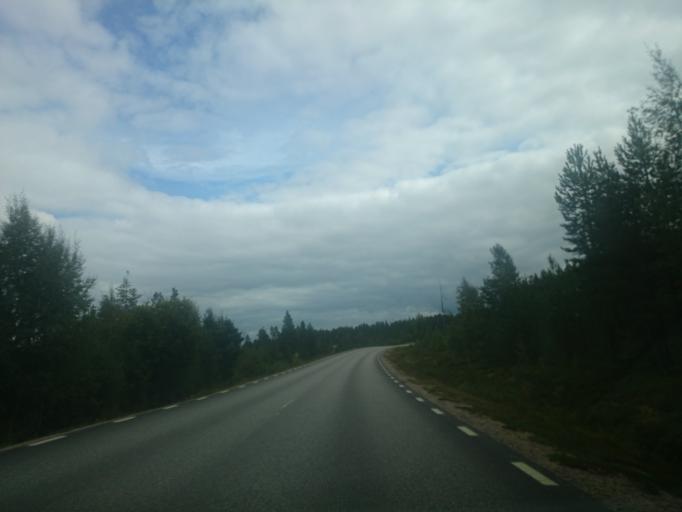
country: SE
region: Jaemtland
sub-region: Harjedalens Kommun
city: Sveg
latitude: 62.0368
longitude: 14.7463
